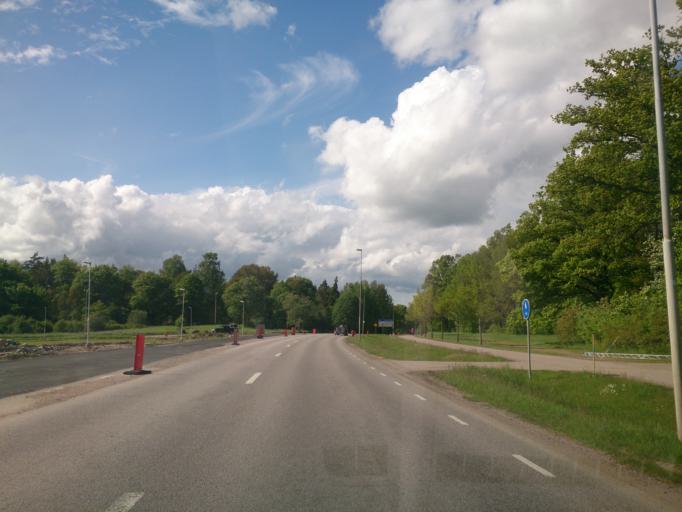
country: SE
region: OEstergoetland
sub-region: Linkopings Kommun
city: Linkoping
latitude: 58.3817
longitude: 15.6327
